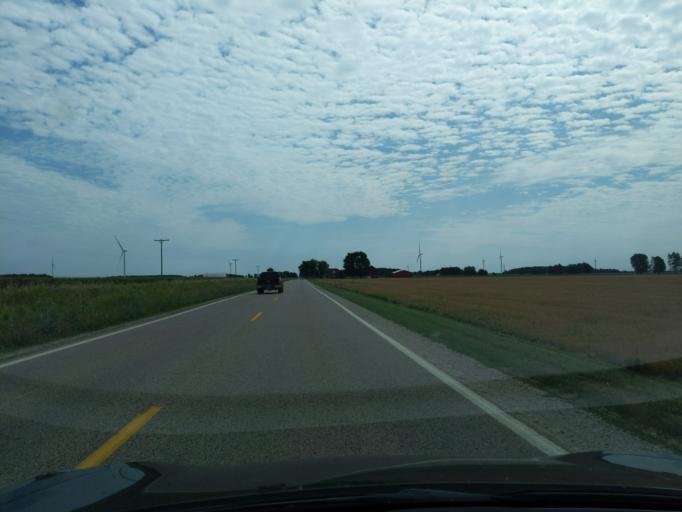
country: US
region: Michigan
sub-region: Gratiot County
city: Ithaca
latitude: 43.2916
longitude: -84.5389
